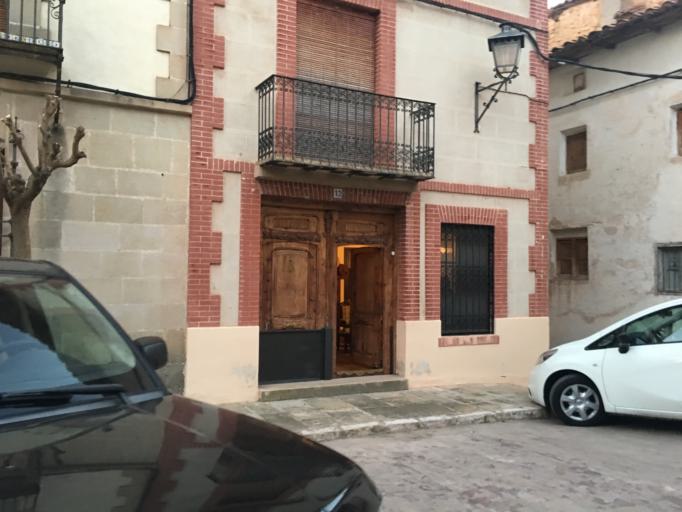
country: ES
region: Aragon
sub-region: Provincia de Teruel
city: Mora de Rubielos
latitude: 40.2530
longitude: -0.7517
